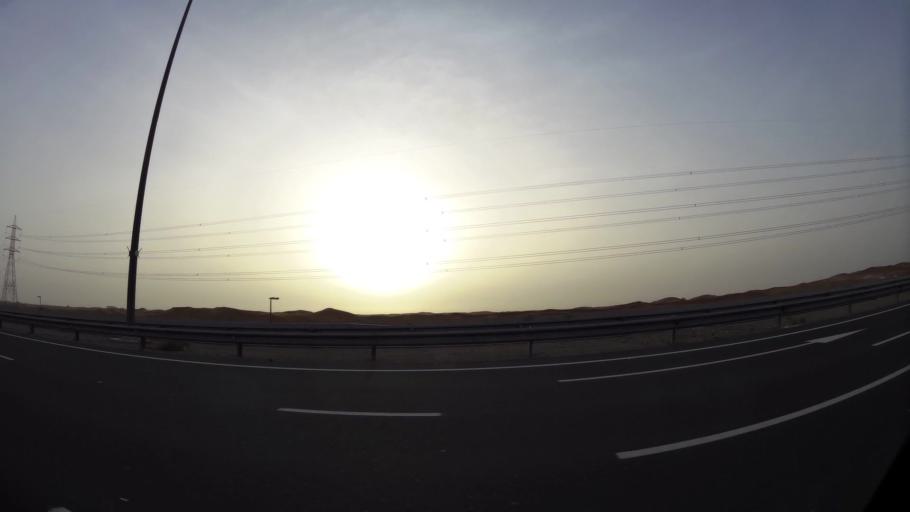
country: OM
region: Al Buraimi
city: Al Buraymi
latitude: 24.3469
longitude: 55.7782
